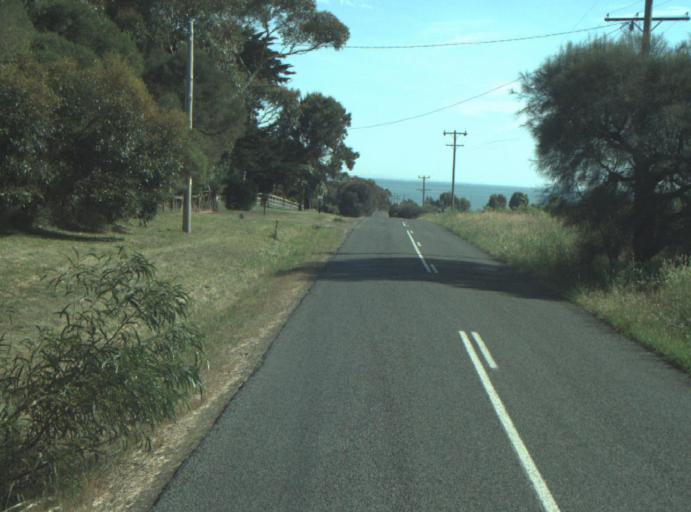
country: AU
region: Victoria
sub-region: Greater Geelong
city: Clifton Springs
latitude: -38.1674
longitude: 144.5156
